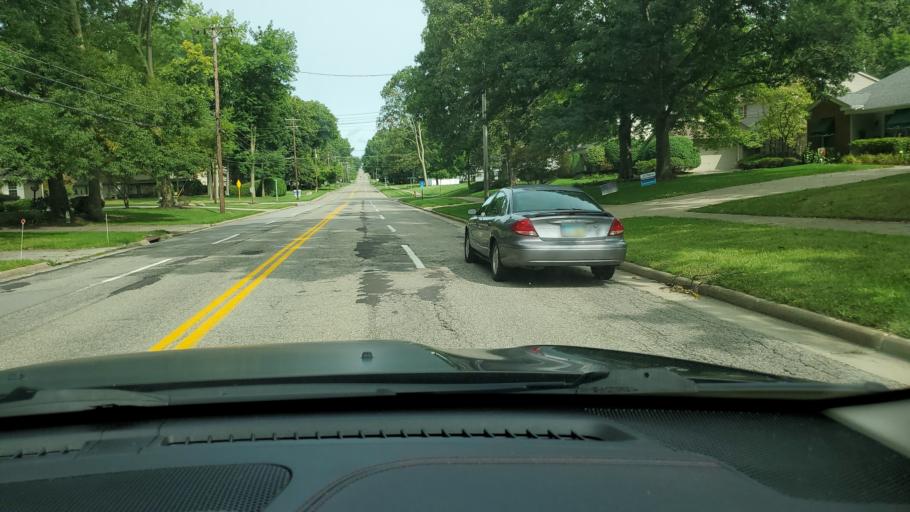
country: US
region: Ohio
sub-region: Mahoning County
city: Boardman
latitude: 41.0008
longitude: -80.6723
